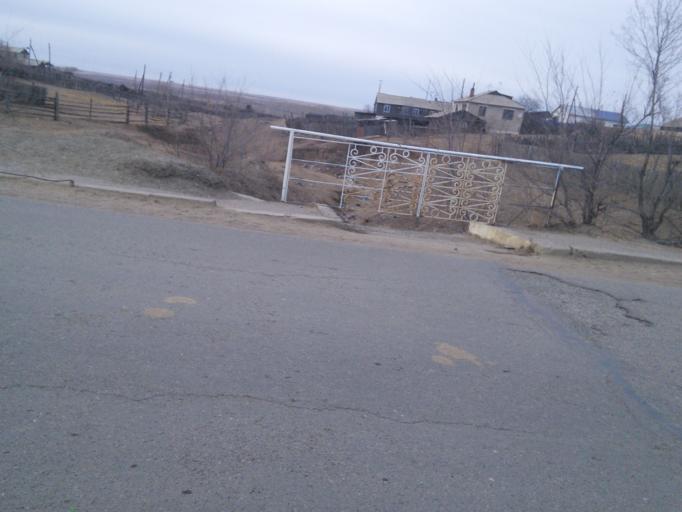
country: RU
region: Transbaikal Territory
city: Nizhniy Tsasuchey
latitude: 50.5109
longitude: 115.1220
